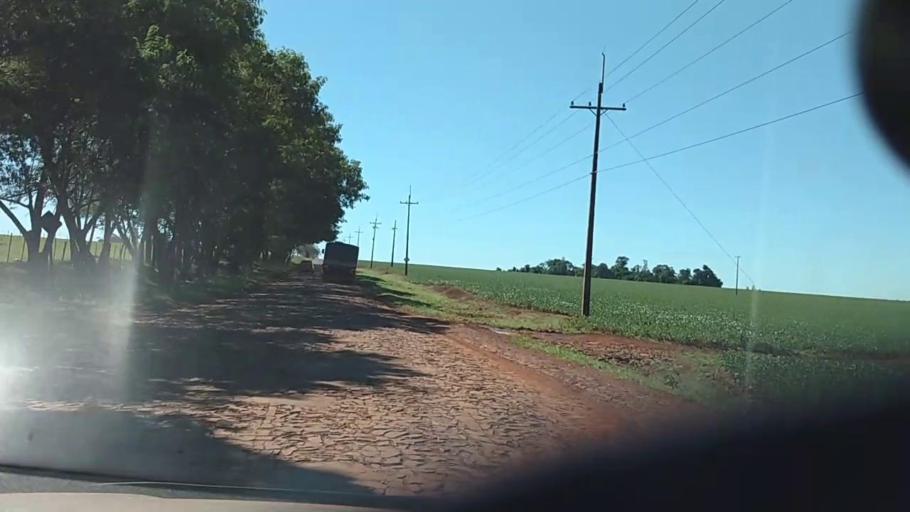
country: PY
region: Alto Parana
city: Naranjal
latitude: -25.9584
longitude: -55.1395
